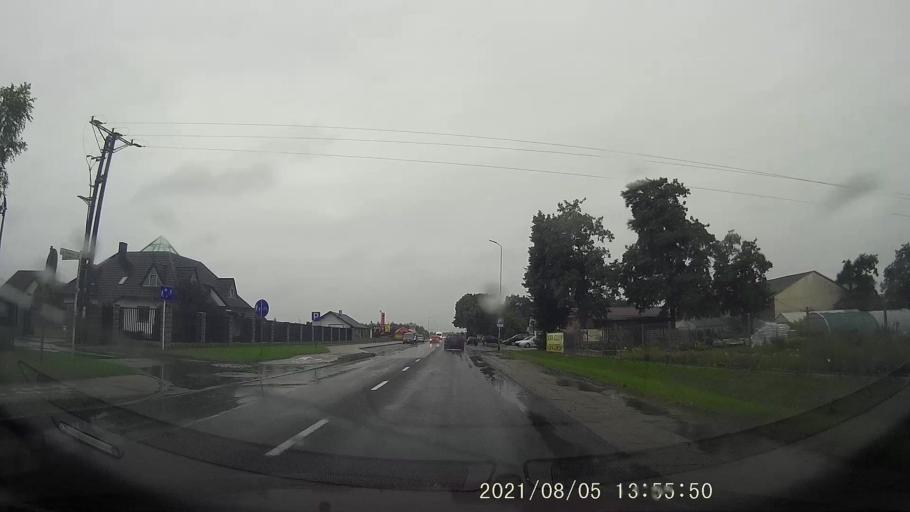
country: PL
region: Opole Voivodeship
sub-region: Powiat krapkowicki
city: Krapkowice
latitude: 50.4669
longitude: 17.9504
